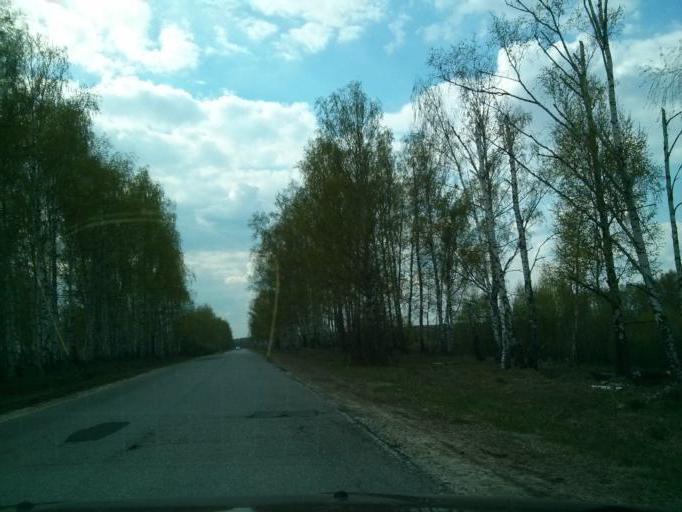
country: RU
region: Vladimir
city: Melenki
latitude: 55.3417
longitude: 41.8272
